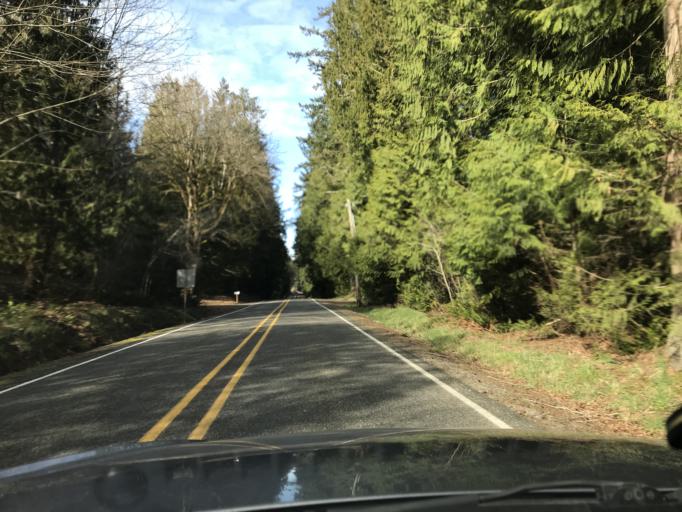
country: US
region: Washington
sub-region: Pierce County
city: Longbranch
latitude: 47.2293
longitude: -122.7905
